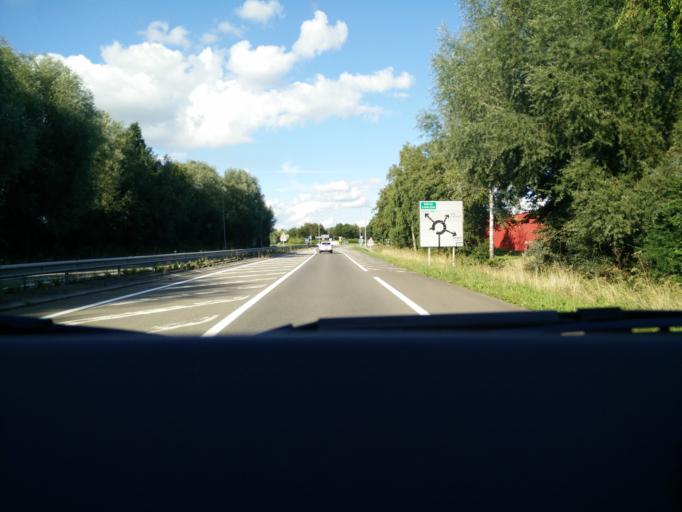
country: FR
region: Nord-Pas-de-Calais
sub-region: Departement du Nord
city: Jeumont
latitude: 50.3060
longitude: 4.0882
